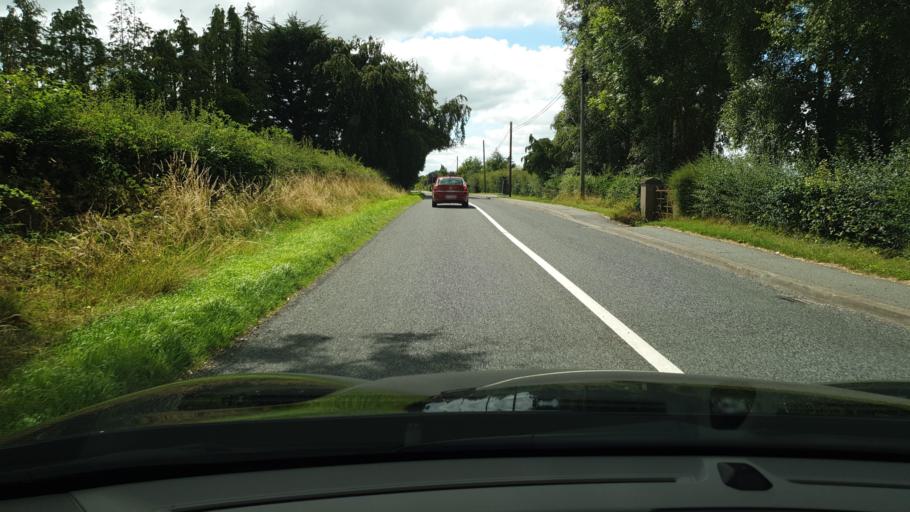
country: IE
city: Kentstown
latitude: 53.5738
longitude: -6.5646
